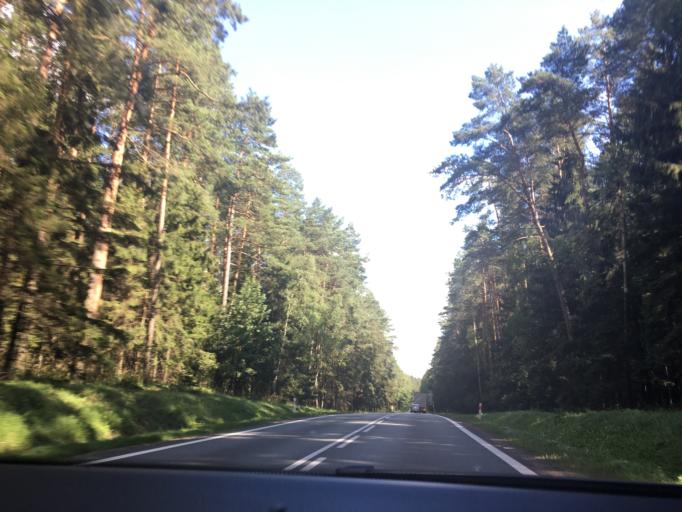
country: PL
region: Podlasie
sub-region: Powiat bialostocki
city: Wasilkow
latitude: 53.2586
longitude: 23.1393
